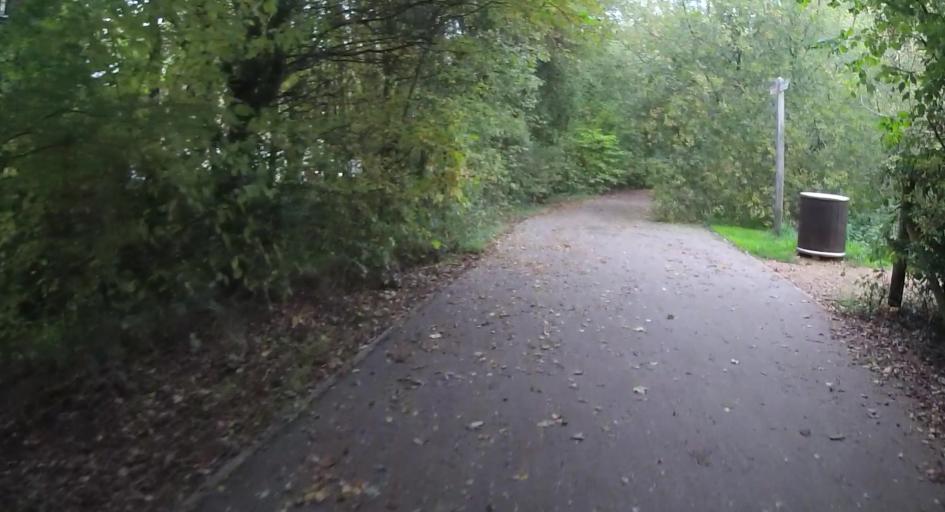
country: GB
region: England
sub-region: Bracknell Forest
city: Binfield
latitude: 51.4051
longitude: -0.7871
